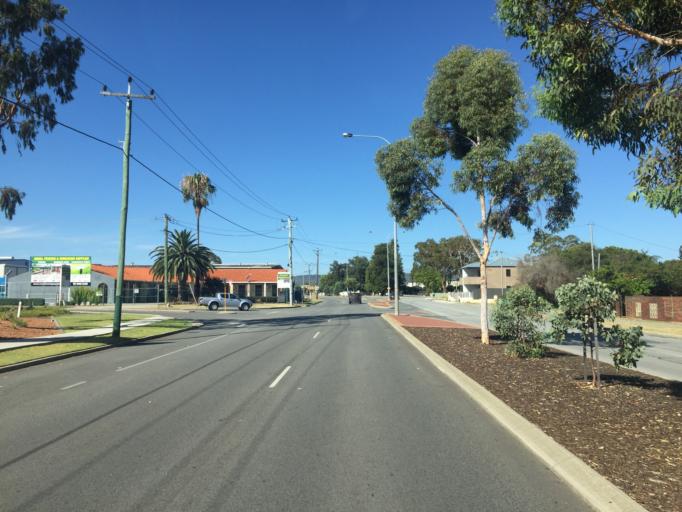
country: AU
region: Western Australia
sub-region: Gosnells
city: Maddington
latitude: -32.0456
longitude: 115.9890
